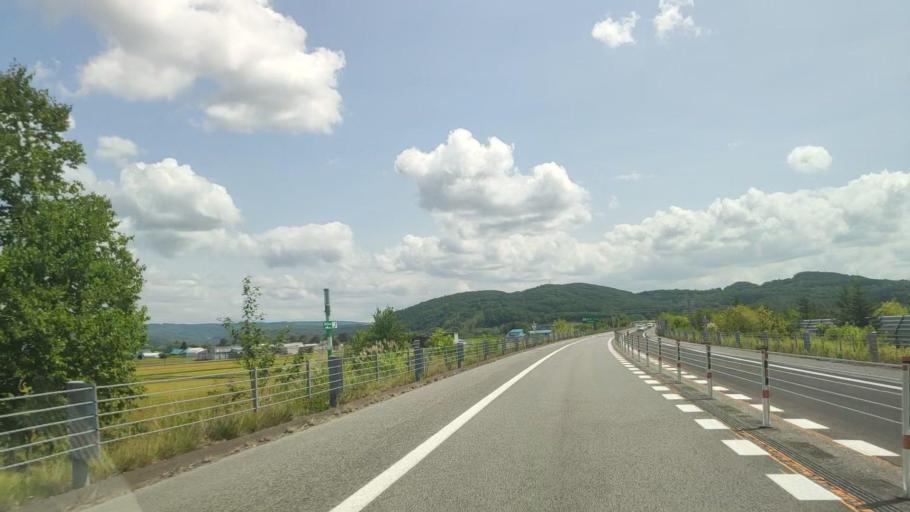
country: JP
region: Hokkaido
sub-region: Asahikawa-shi
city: Asahikawa
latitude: 43.9052
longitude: 142.5469
